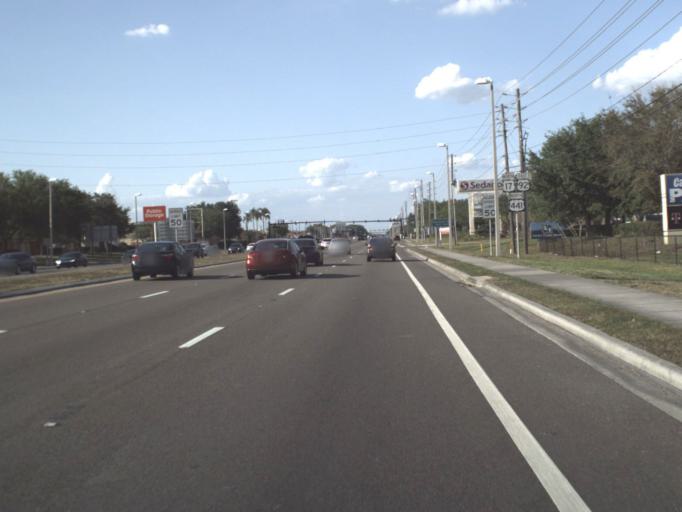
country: US
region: Florida
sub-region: Orange County
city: Hunters Creek
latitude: 28.3758
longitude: -81.4044
